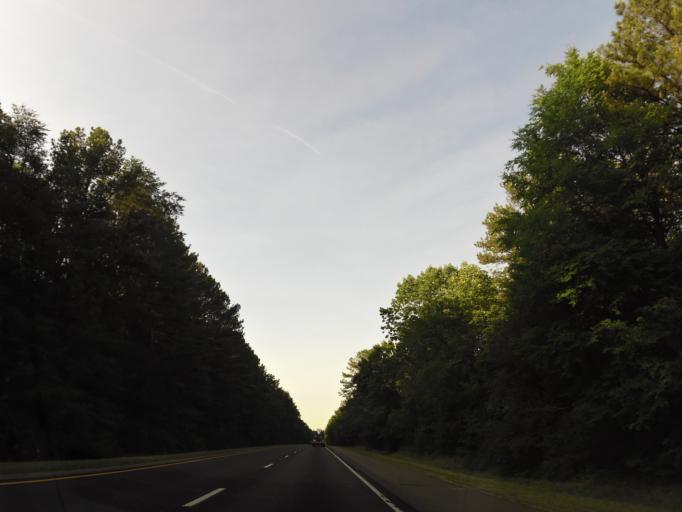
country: US
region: Alabama
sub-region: DeKalb County
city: Fort Payne
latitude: 34.4037
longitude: -85.7804
